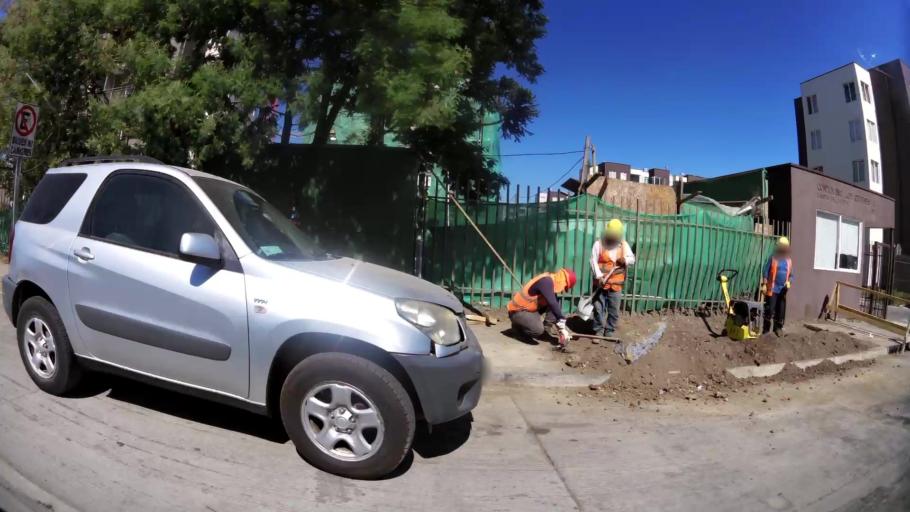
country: CL
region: Biobio
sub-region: Provincia de Concepcion
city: Concepcion
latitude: -36.7899
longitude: -73.0345
